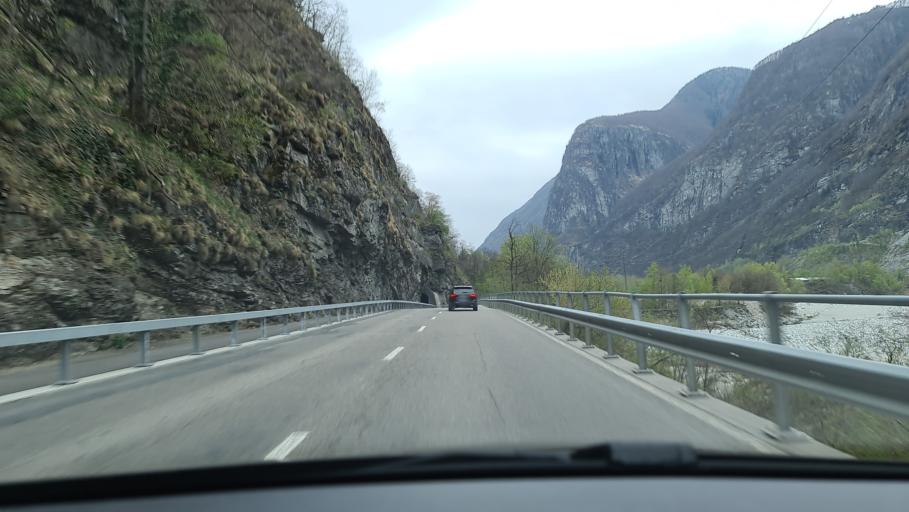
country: CH
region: Ticino
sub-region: Vallemaggia District
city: Cevio
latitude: 46.3059
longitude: 8.6149
